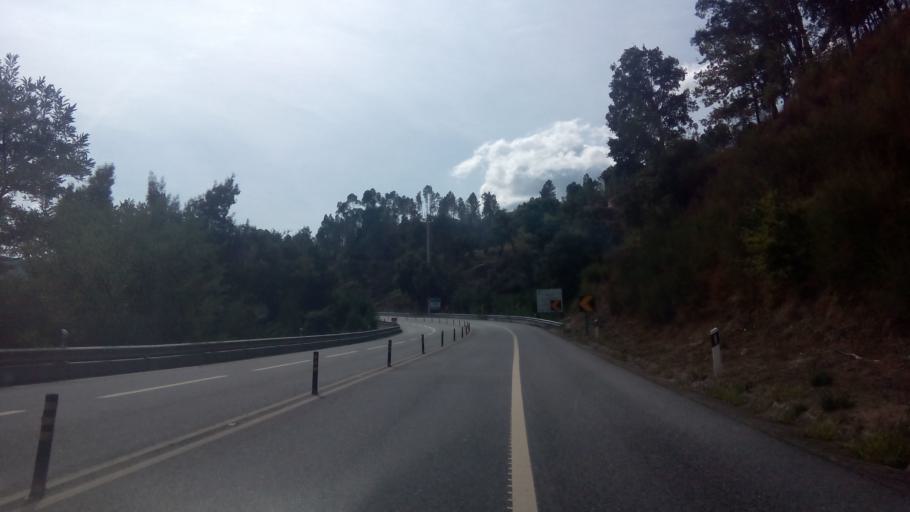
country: PT
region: Porto
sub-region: Amarante
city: Amarante
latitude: 41.2625
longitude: -8.0303
